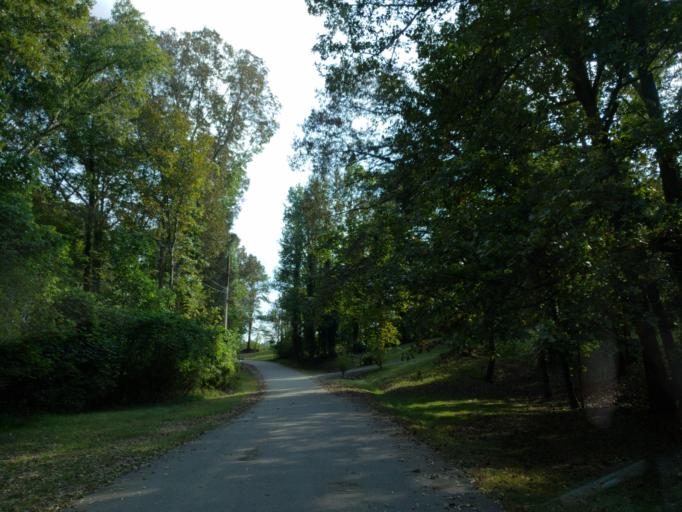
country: US
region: Georgia
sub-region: Fulton County
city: Roswell
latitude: 34.0861
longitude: -84.4216
